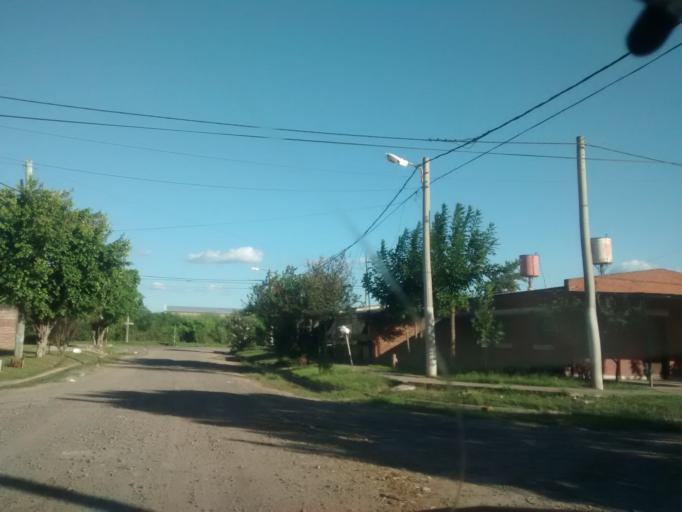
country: AR
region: Chaco
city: Fontana
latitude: -27.4600
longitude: -59.0316
